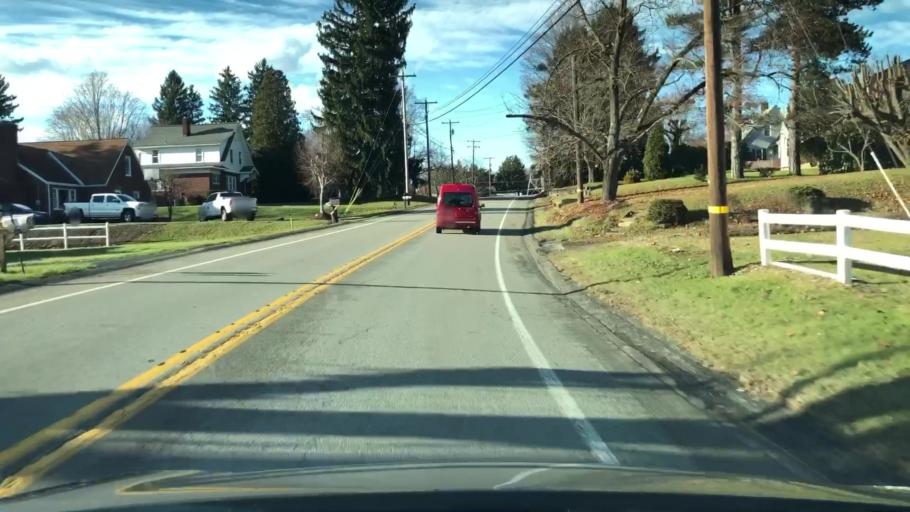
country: US
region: Pennsylvania
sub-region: Butler County
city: Meadowood
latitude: 40.8413
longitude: -79.8717
